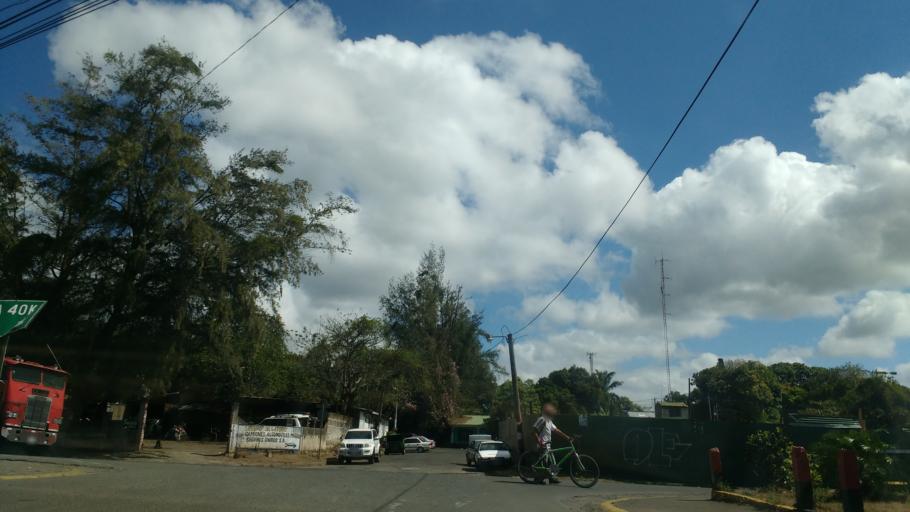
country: NI
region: Carazo
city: Diriamba
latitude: 11.8622
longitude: -86.2398
